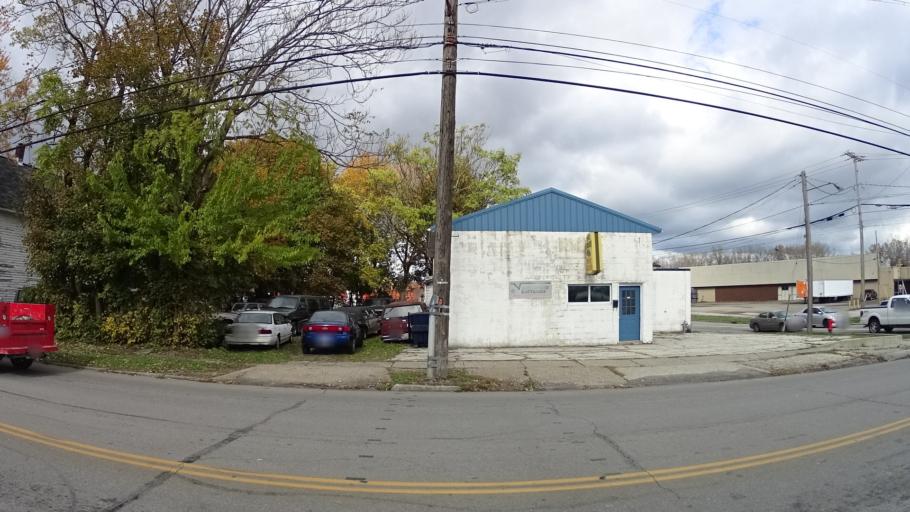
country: US
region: Ohio
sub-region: Lorain County
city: Lorain
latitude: 41.4517
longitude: -82.1644
